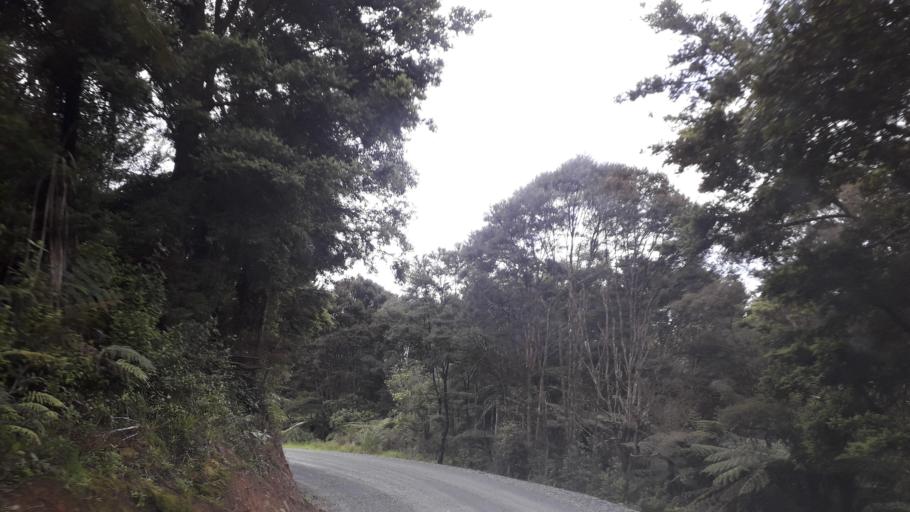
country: NZ
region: Northland
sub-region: Far North District
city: Taipa
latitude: -35.0591
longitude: 173.5510
